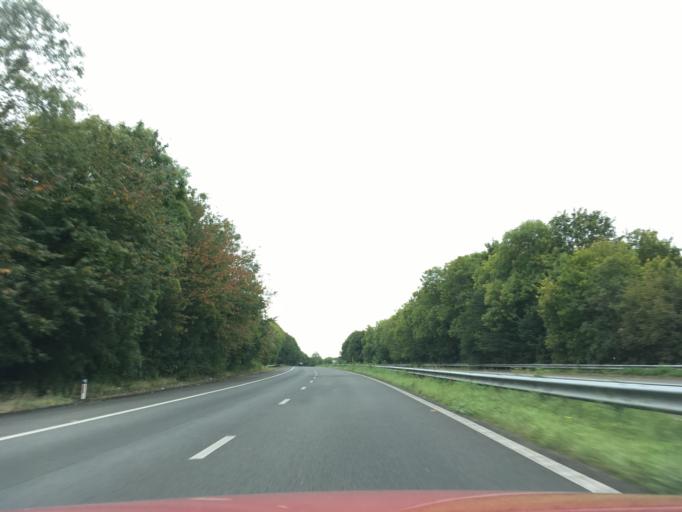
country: GB
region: Wales
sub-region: Monmouthshire
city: Caldicot
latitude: 51.6107
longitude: -2.7351
